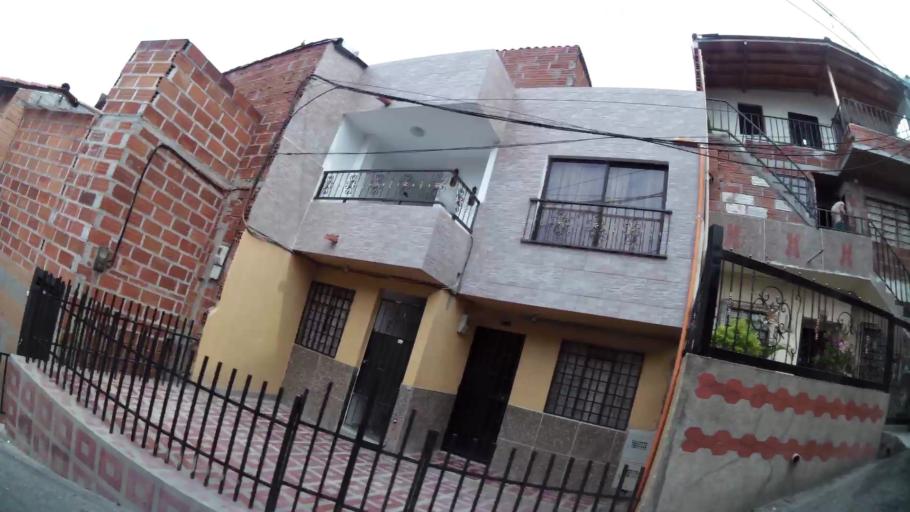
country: CO
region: Antioquia
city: Medellin
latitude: 6.2892
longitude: -75.5537
